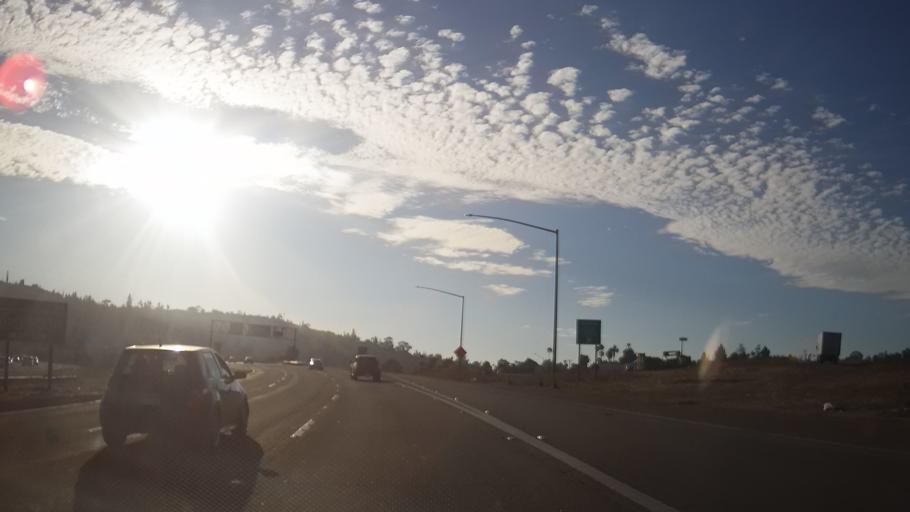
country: US
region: California
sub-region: San Diego County
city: Spring Valley
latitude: 32.7532
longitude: -117.0045
